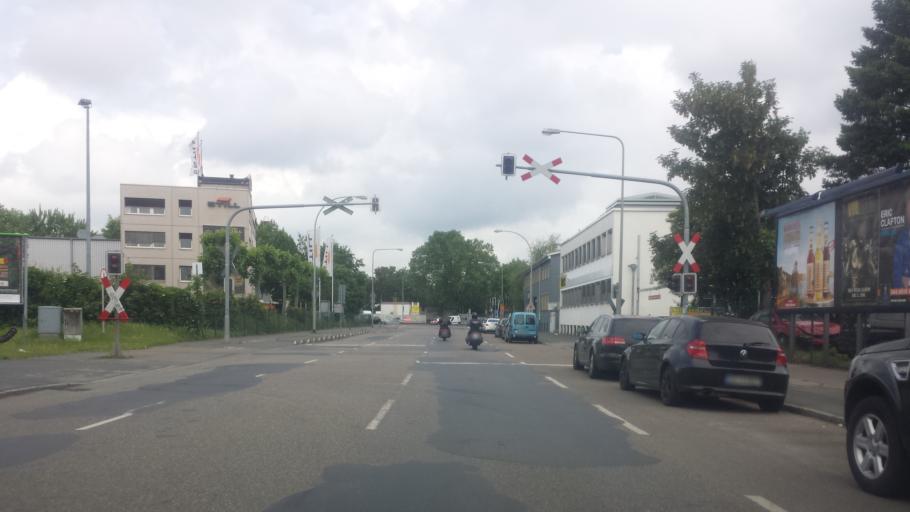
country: DE
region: Hesse
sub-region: Regierungsbezirk Darmstadt
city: Offenbach
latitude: 50.1224
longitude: 8.7474
